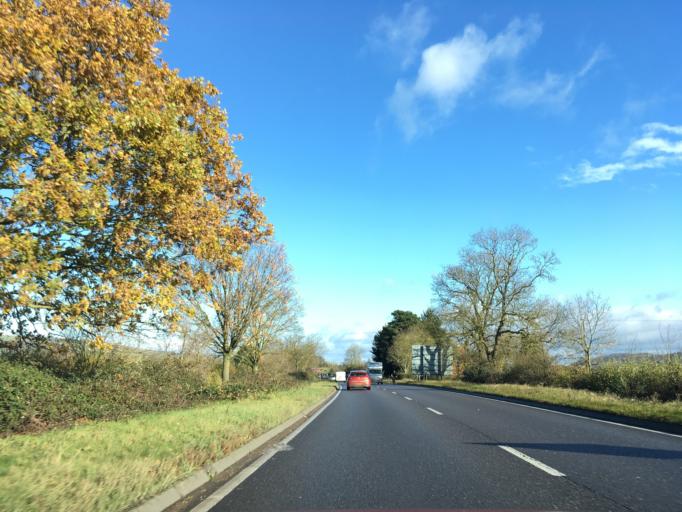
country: GB
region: England
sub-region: Gloucestershire
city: Gotherington
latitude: 52.0053
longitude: -2.0513
